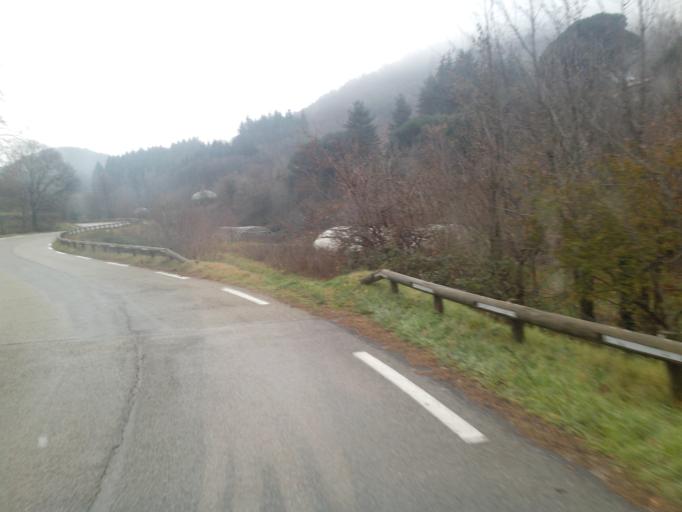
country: FR
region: Languedoc-Roussillon
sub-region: Departement du Gard
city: Lasalle
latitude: 44.0266
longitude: 3.8554
